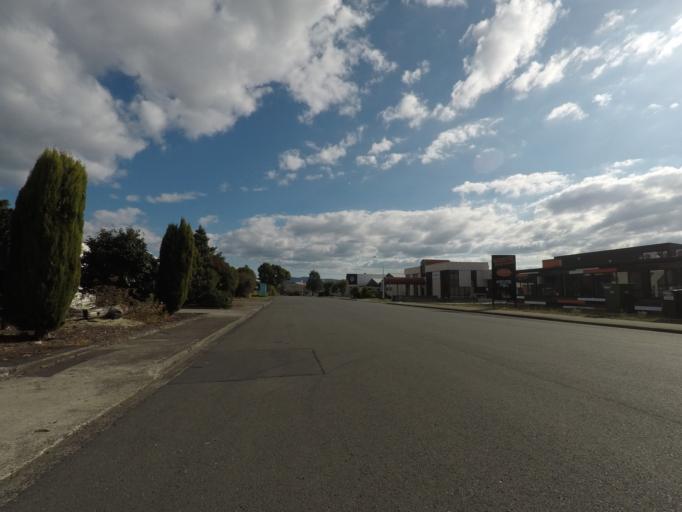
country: NZ
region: Auckland
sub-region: Auckland
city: Rosebank
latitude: -36.8765
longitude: 174.6687
